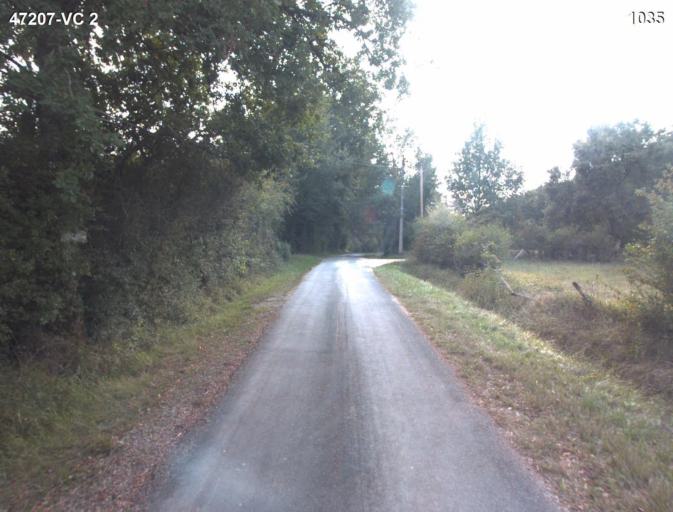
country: FR
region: Aquitaine
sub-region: Departement du Lot-et-Garonne
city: Barbaste
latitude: 44.1859
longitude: 0.2266
